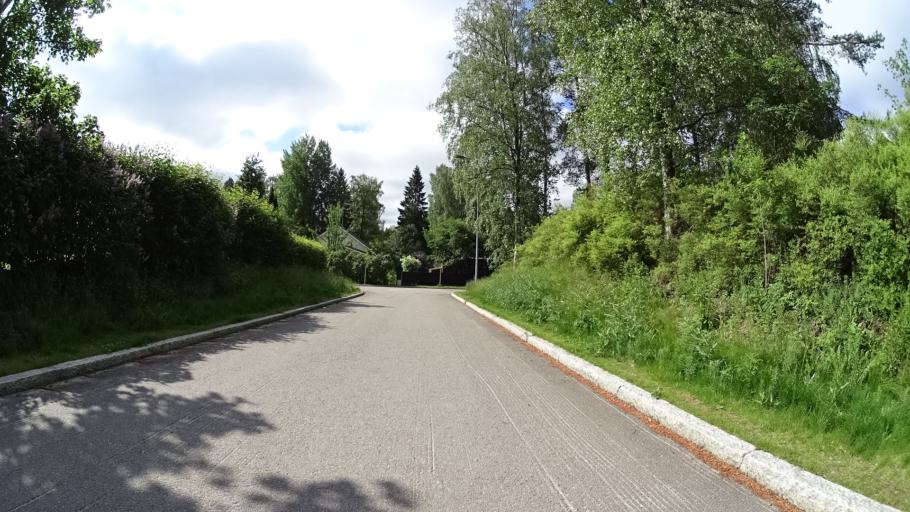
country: FI
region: Uusimaa
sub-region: Helsinki
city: Teekkarikylae
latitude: 60.2273
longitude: 24.8387
